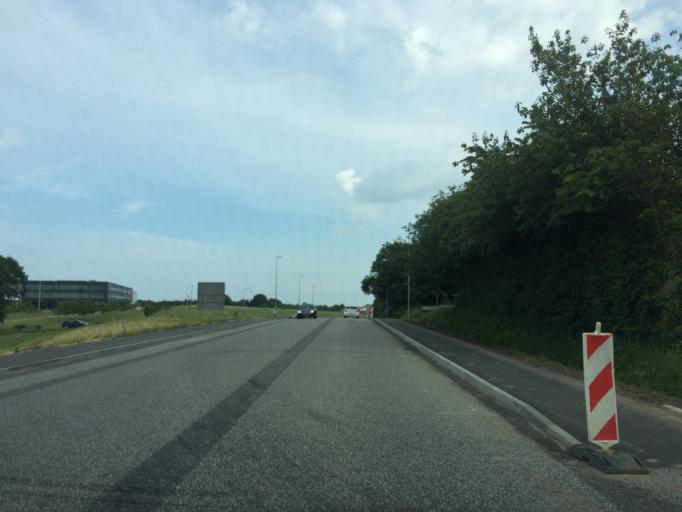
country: DK
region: South Denmark
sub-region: Fredericia Kommune
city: Snoghoj
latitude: 55.5343
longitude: 9.6949
